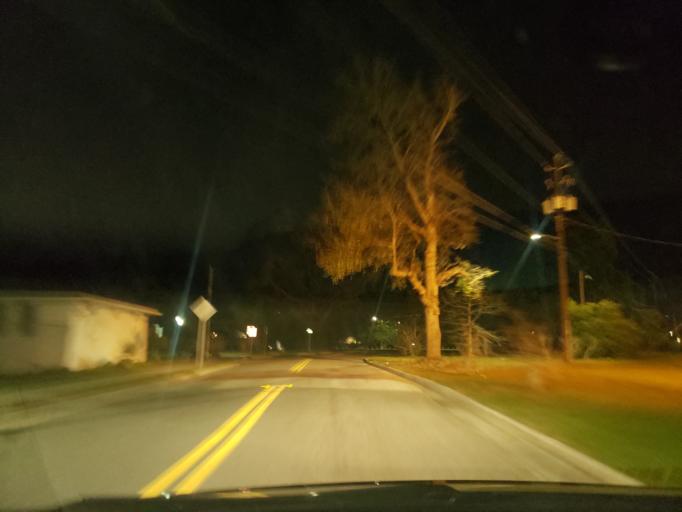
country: US
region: Georgia
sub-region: Chatham County
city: Savannah
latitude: 32.0432
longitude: -81.1125
